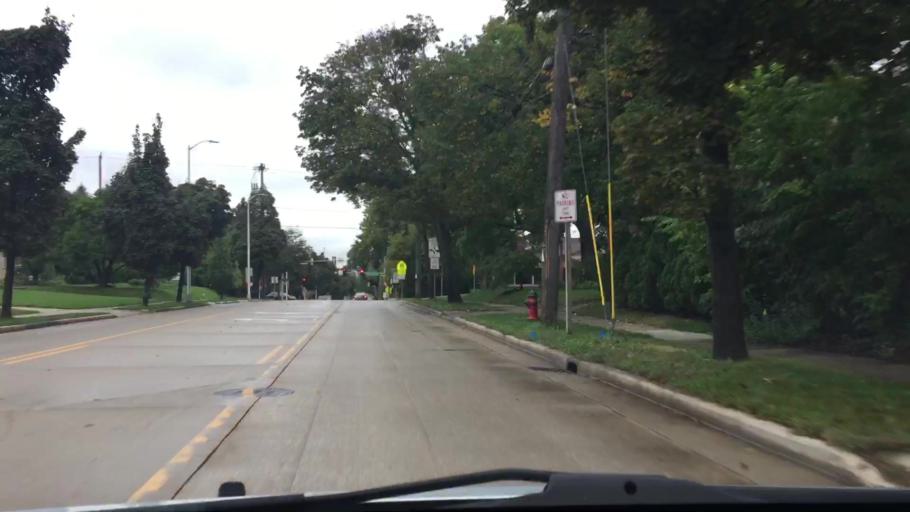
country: US
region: Wisconsin
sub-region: Milwaukee County
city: Wauwatosa
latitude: 43.0370
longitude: -88.0157
